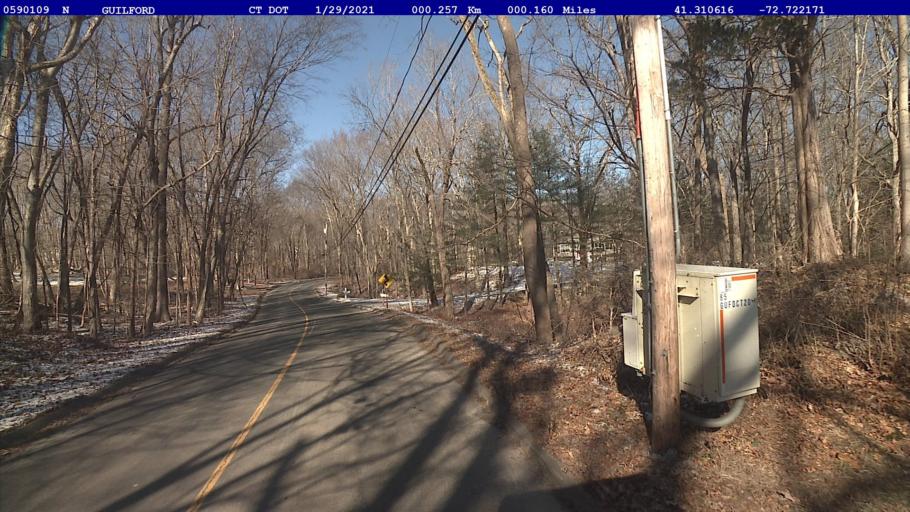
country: US
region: Connecticut
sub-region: New Haven County
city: Guilford
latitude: 41.3106
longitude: -72.7222
